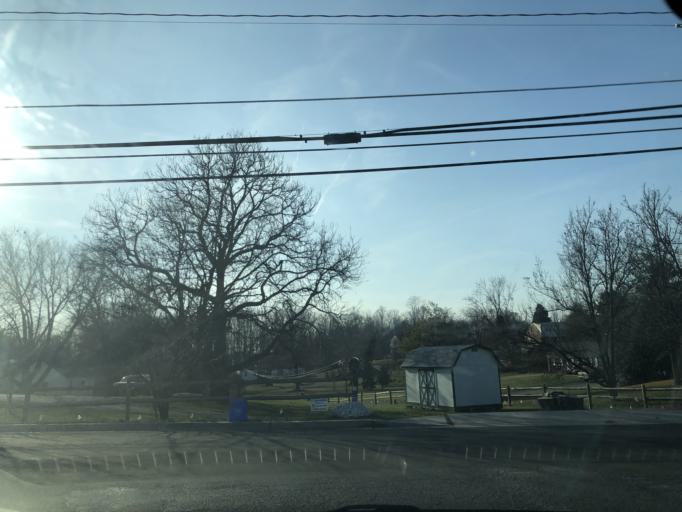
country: US
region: Maryland
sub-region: Montgomery County
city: Burtonsville
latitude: 39.1054
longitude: -76.9338
